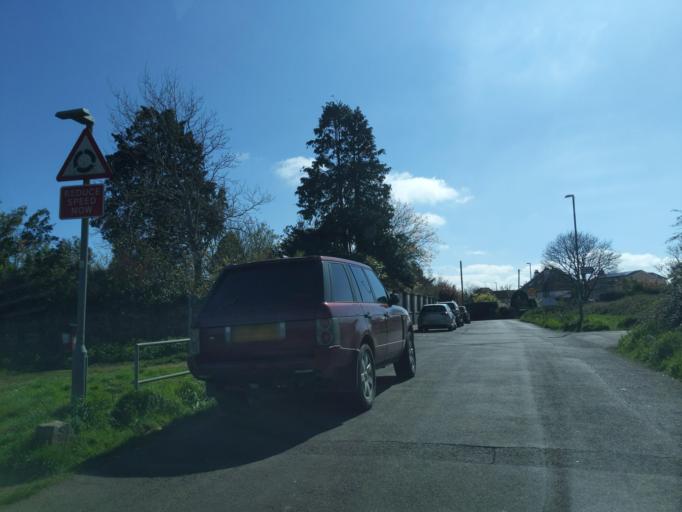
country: GB
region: England
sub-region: Borough of Torbay
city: Paignton
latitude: 50.4007
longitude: -3.5664
